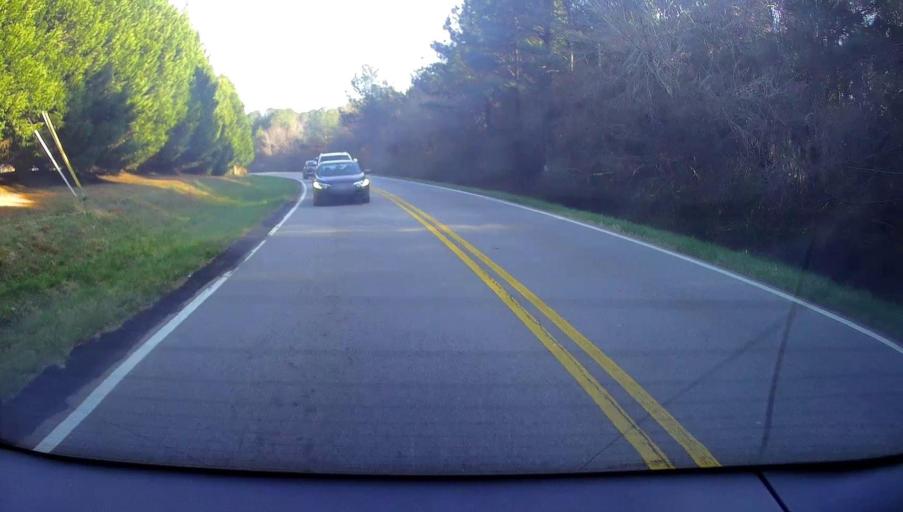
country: US
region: Georgia
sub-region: Henry County
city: Locust Grove
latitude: 33.3612
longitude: -84.1761
